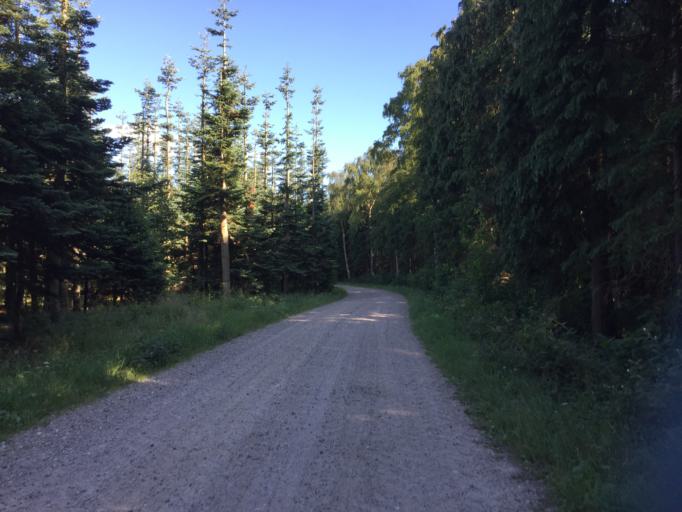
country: DK
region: South Denmark
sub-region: Kerteminde Kommune
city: Langeskov
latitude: 55.3601
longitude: 10.5529
